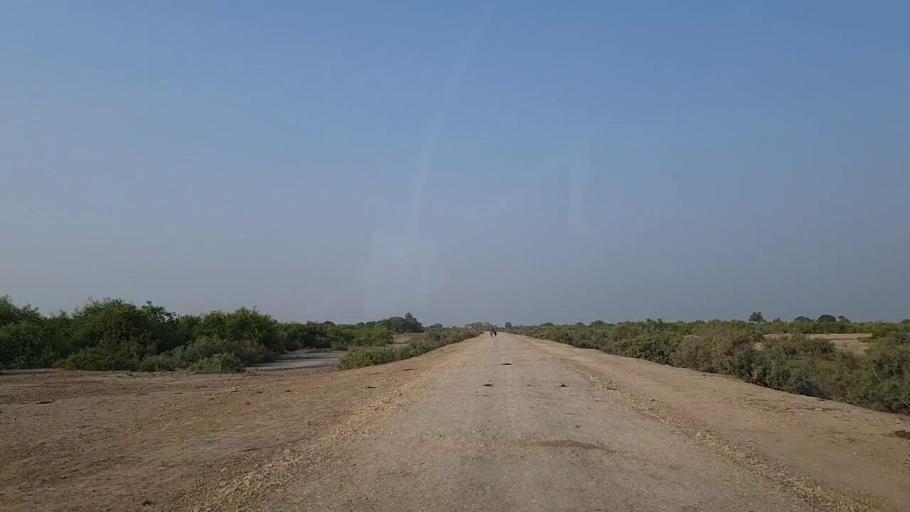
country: PK
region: Sindh
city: Mirpur Sakro
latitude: 24.6398
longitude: 67.7674
